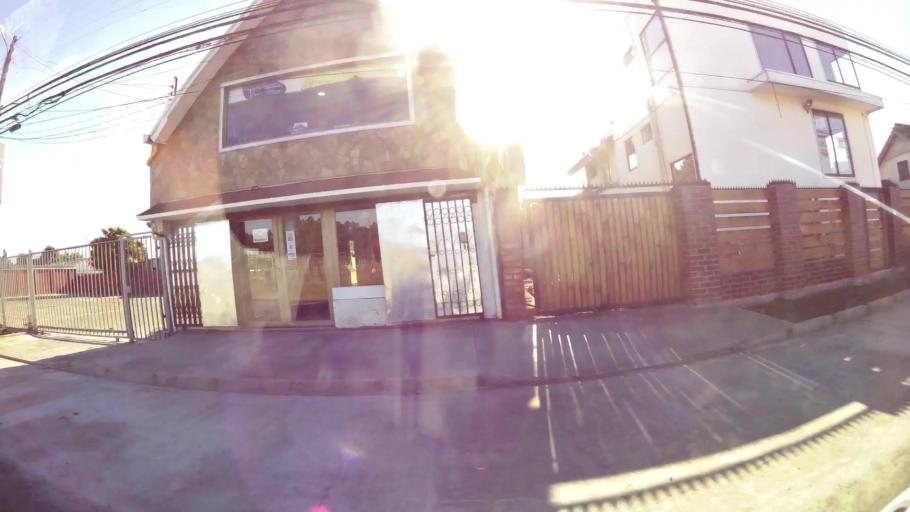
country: CL
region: Biobio
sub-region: Provincia de Concepcion
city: Concepcion
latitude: -36.8343
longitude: -73.1021
